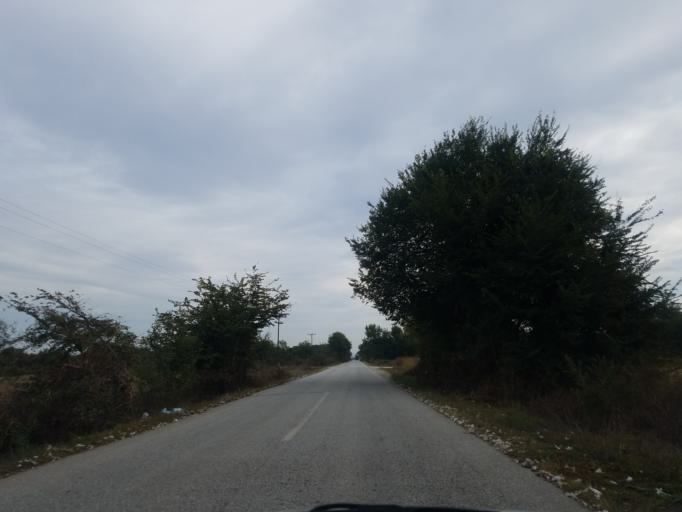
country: GR
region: Thessaly
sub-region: Nomos Kardhitsas
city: Agia Triada
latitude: 39.4615
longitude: 21.8788
